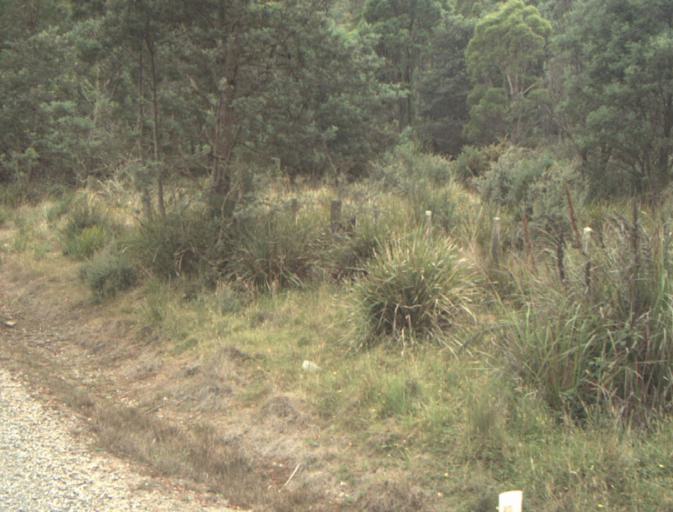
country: AU
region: Tasmania
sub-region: Northern Midlands
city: Evandale
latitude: -41.4622
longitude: 147.4958
